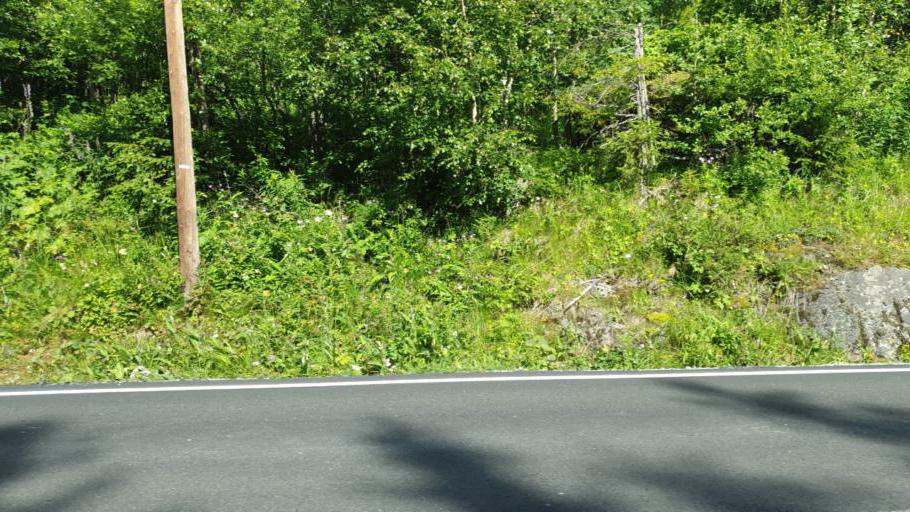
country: NO
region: Oppland
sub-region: Oystre Slidre
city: Heggenes
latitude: 61.1662
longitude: 8.9964
